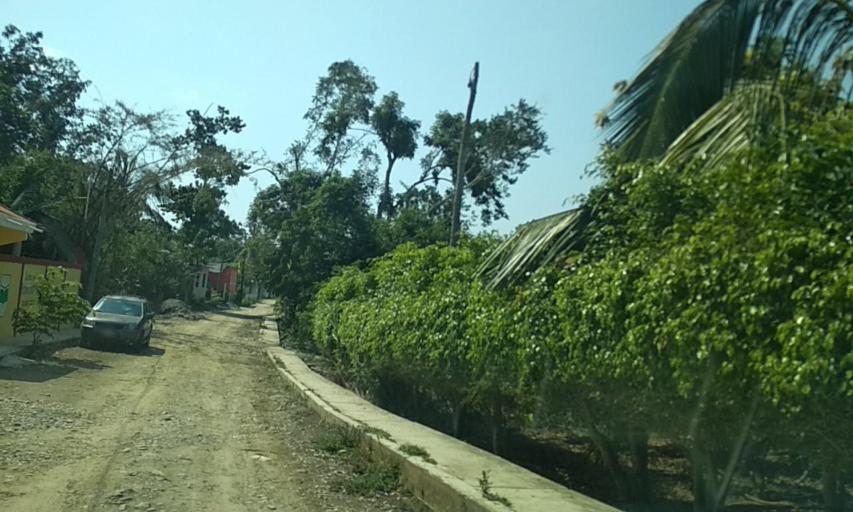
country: MX
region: Veracruz
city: Gutierrez Zamora
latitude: 20.3617
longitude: -97.1678
